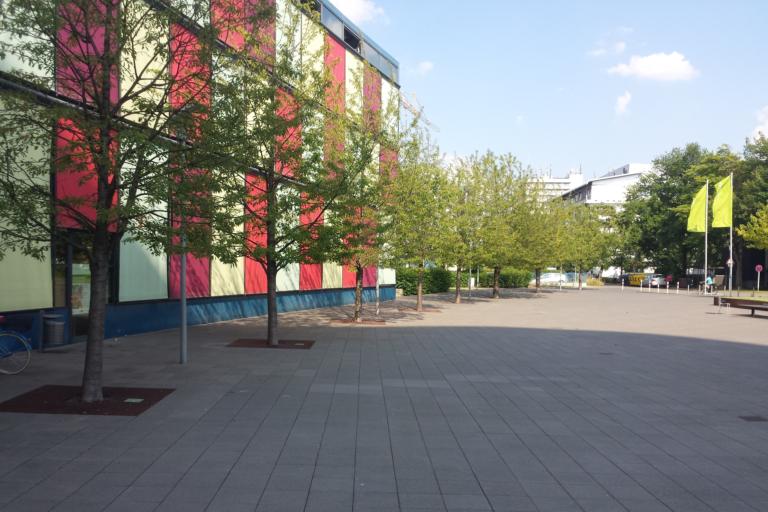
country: DE
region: Baden-Wuerttemberg
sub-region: Karlsruhe Region
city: Eppelheim
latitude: 49.4139
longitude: 8.6512
